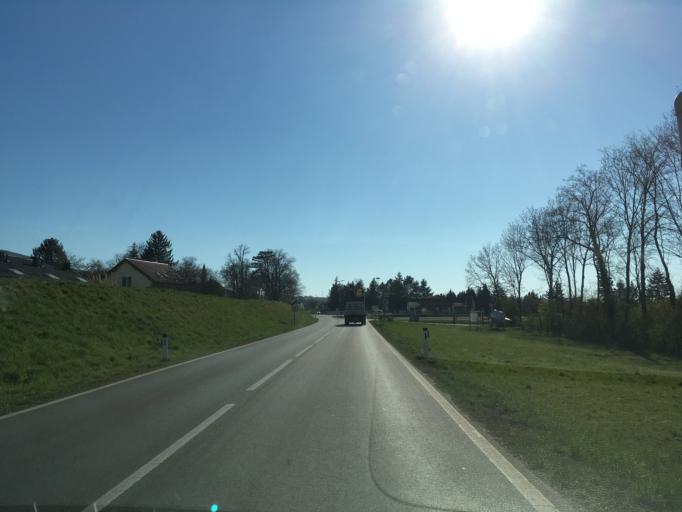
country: AT
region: Lower Austria
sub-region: Politischer Bezirk Tulln
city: Konigstetten
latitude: 48.3065
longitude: 16.1594
